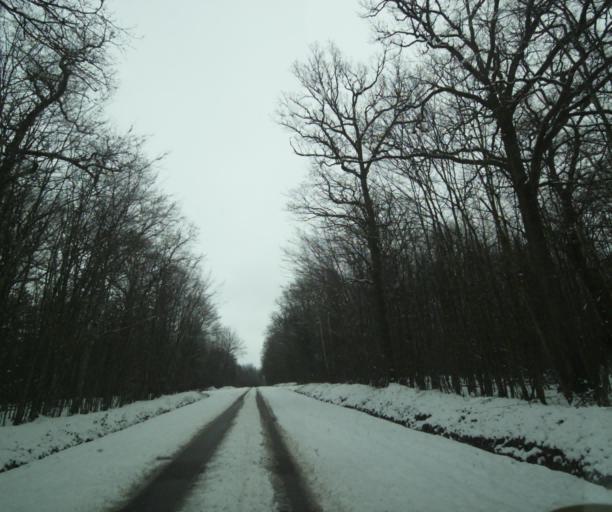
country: FR
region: Champagne-Ardenne
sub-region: Departement de la Haute-Marne
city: Montier-en-Der
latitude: 48.4208
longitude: 4.7731
